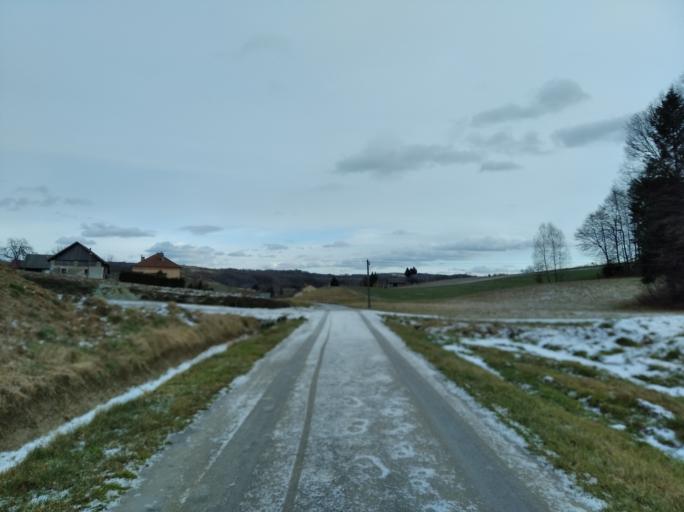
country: PL
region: Subcarpathian Voivodeship
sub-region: Powiat strzyzowski
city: Wysoka Strzyzowska
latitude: 49.9026
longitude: 21.7237
